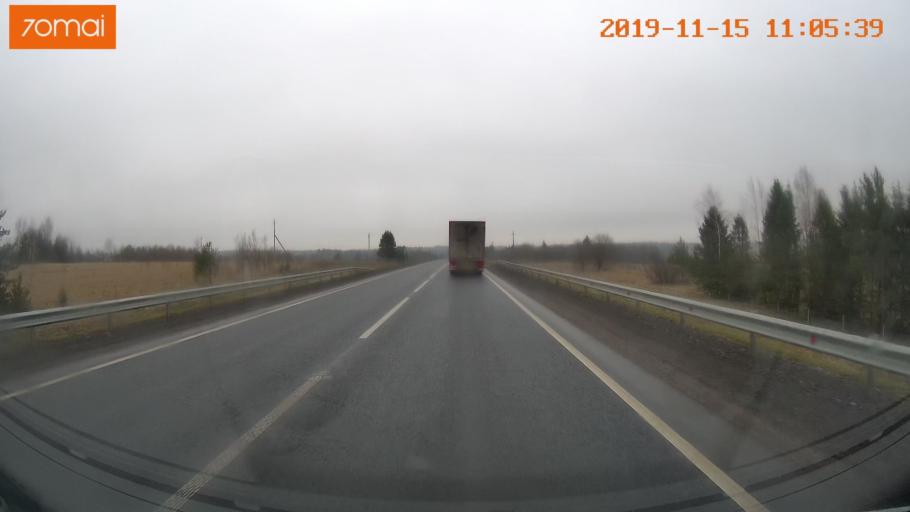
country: RU
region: Vologda
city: Chebsara
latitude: 59.1185
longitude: 39.0083
